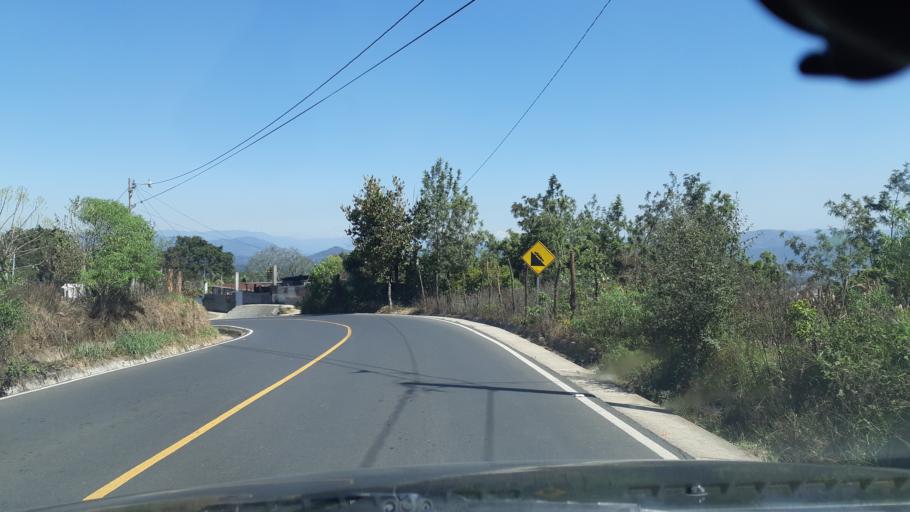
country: GT
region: Chimaltenango
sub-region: Municipio de Zaragoza
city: Zaragoza
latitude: 14.6652
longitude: -90.8614
